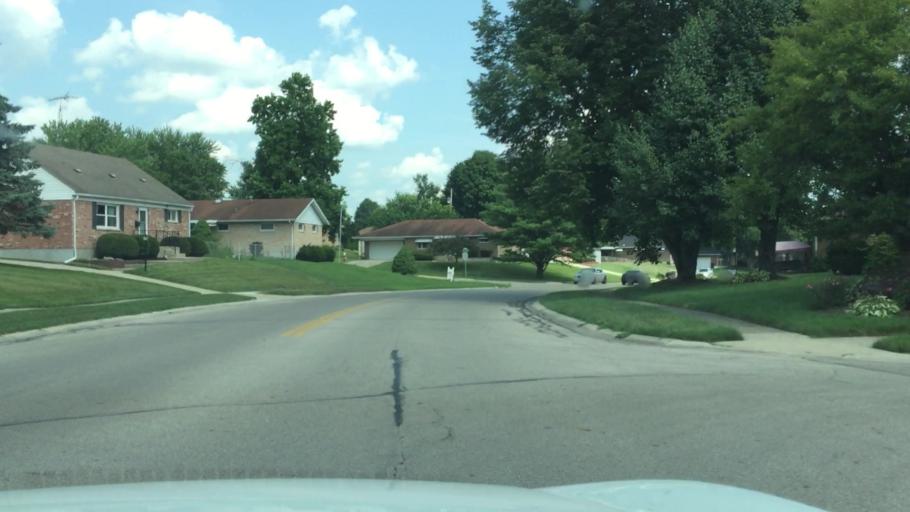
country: US
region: Ohio
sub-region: Clark County
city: Northridge
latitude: 39.9845
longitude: -83.7813
